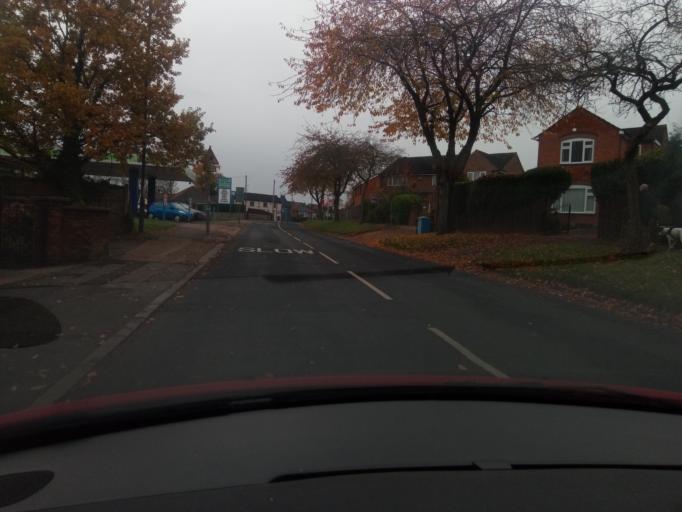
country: GB
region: England
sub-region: Derby
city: Derby
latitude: 52.9316
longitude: -1.4305
